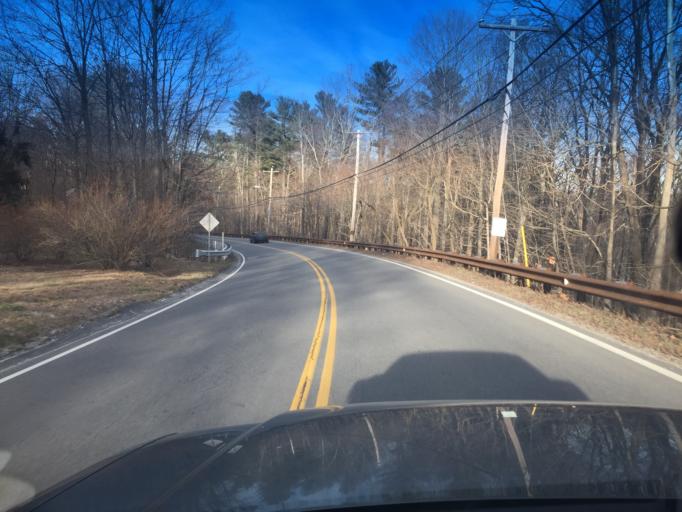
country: US
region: Massachusetts
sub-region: Middlesex County
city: Sherborn
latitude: 42.2327
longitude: -71.3811
